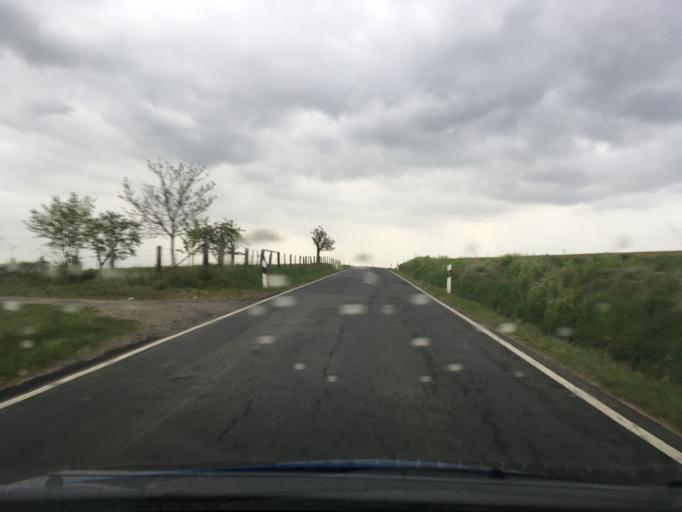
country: DE
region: Lower Saxony
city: Eimen
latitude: 51.8595
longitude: 9.8080
